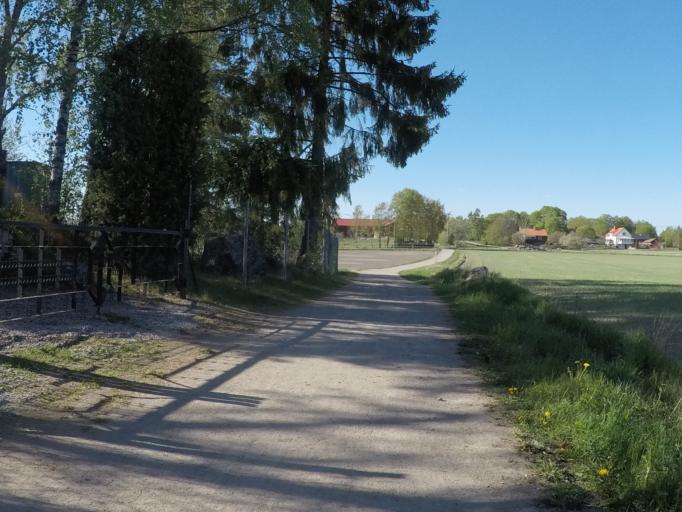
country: SE
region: Soedermanland
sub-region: Eskilstuna Kommun
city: Eskilstuna
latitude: 59.3971
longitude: 16.5276
